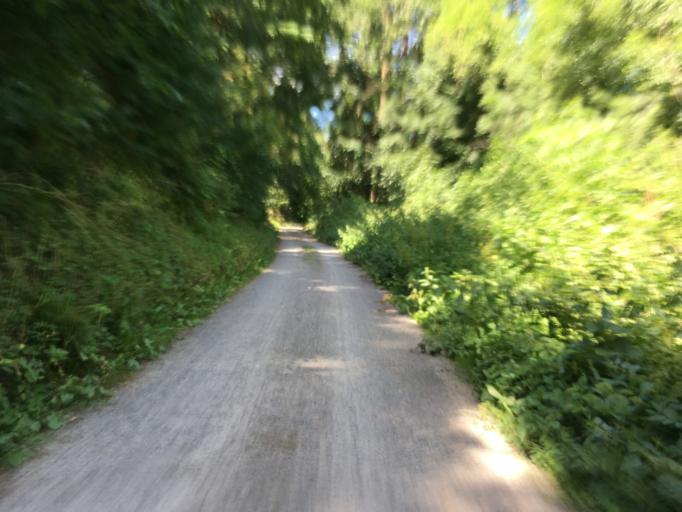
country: DE
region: Baden-Wuerttemberg
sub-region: Regierungsbezirk Stuttgart
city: Vaihingen an der Enz
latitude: 48.9160
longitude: 8.9582
